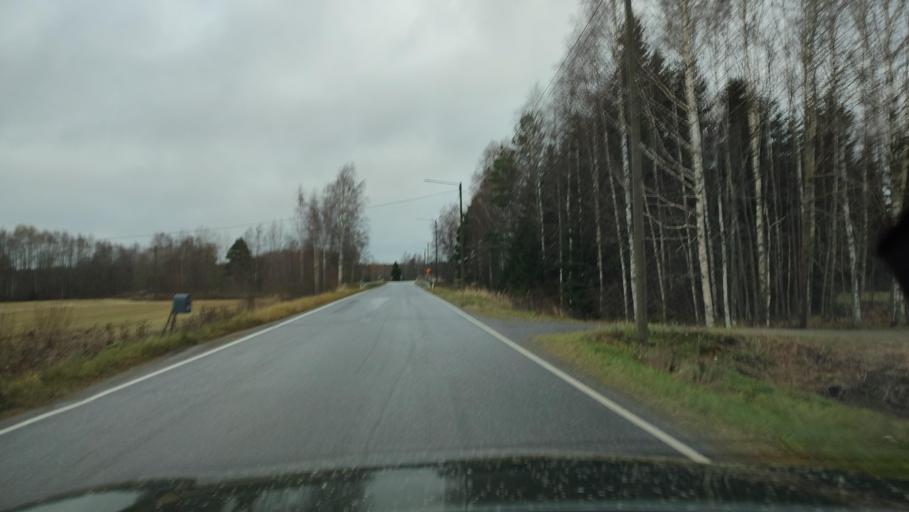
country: FI
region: Southern Ostrobothnia
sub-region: Suupohja
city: Teuva
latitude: 62.4587
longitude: 21.6048
